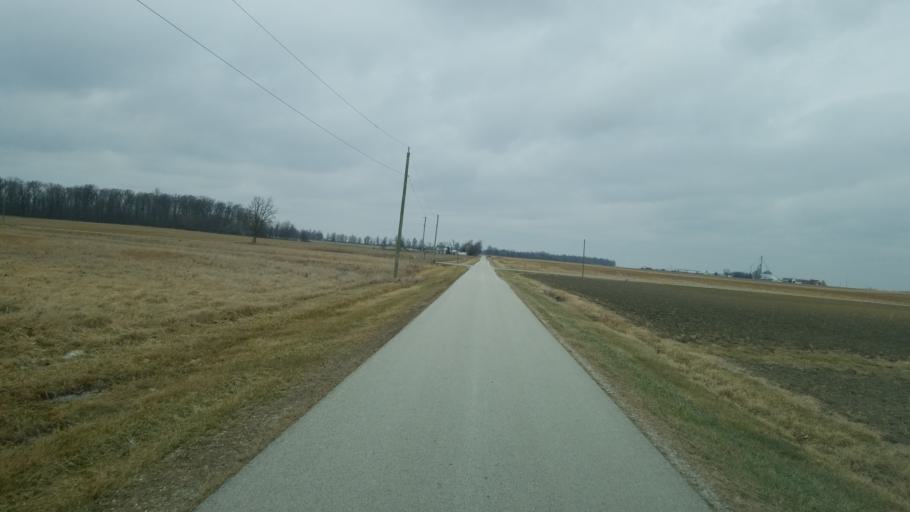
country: US
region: Ohio
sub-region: Hardin County
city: Forest
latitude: 40.7730
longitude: -83.4777
